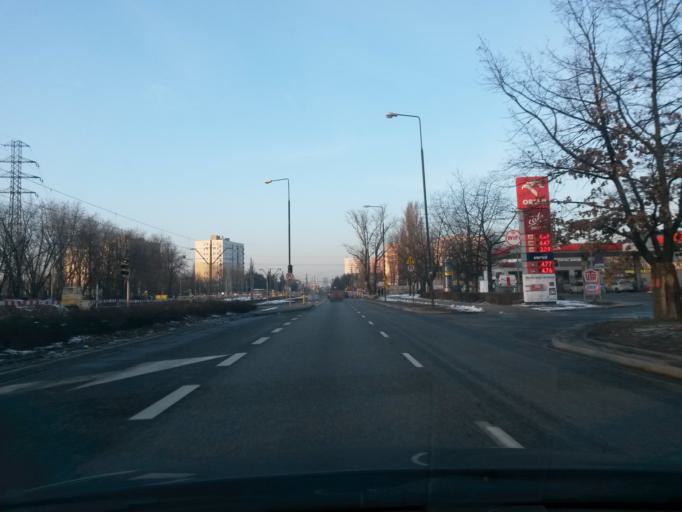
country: PL
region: Masovian Voivodeship
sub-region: Warszawa
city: Mokotow
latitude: 52.1867
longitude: 21.0023
